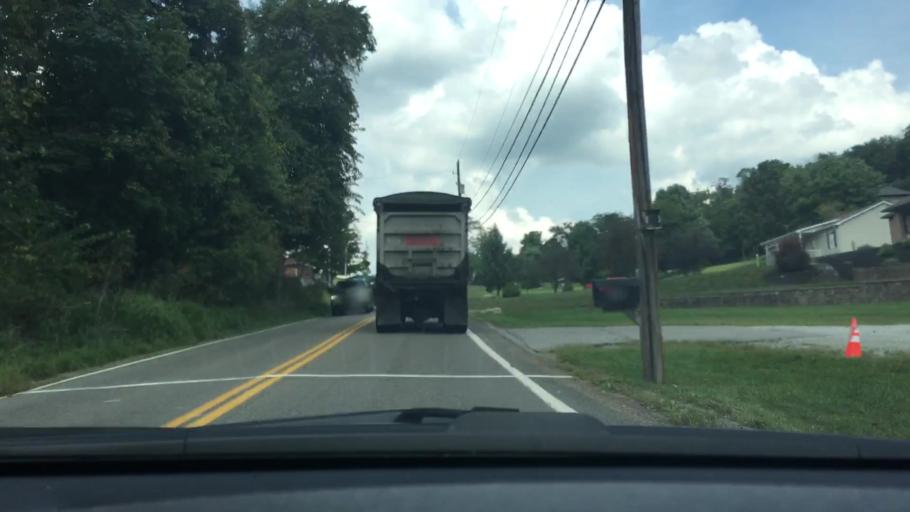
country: US
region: Pennsylvania
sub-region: Washington County
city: Gastonville
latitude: 40.2539
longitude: -79.9748
